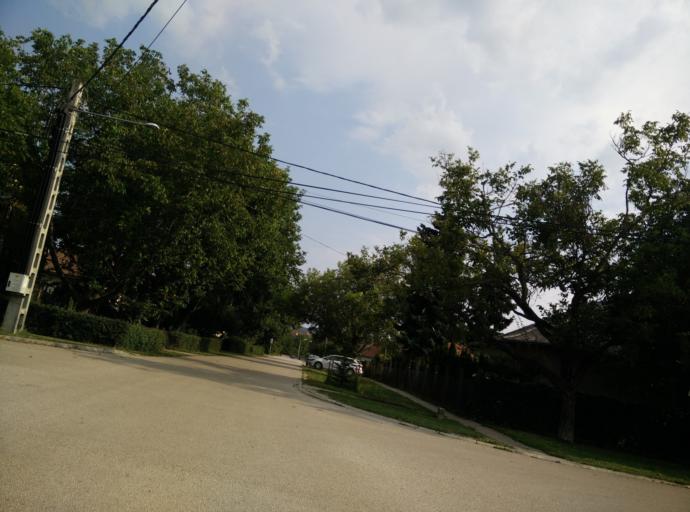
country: HU
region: Pest
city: Paty
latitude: 47.5182
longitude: 18.8286
